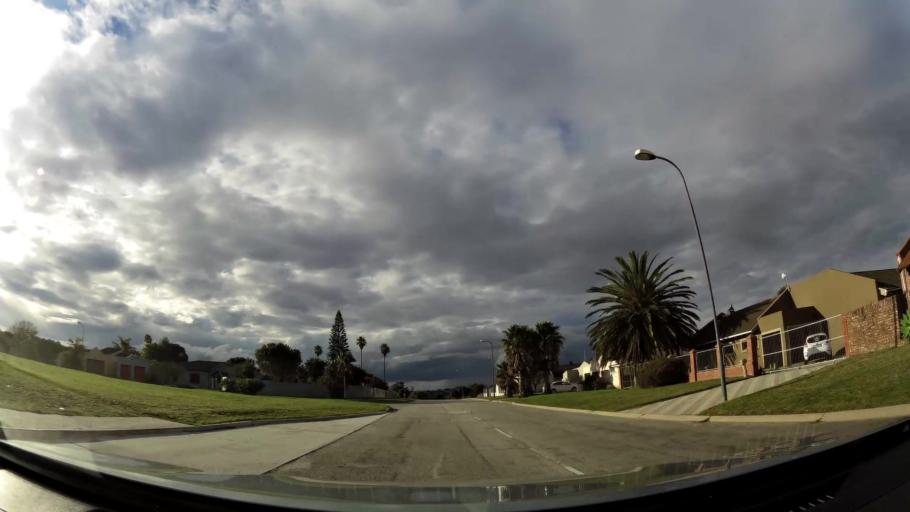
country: ZA
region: Eastern Cape
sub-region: Nelson Mandela Bay Metropolitan Municipality
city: Port Elizabeth
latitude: -33.9566
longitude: 25.4802
